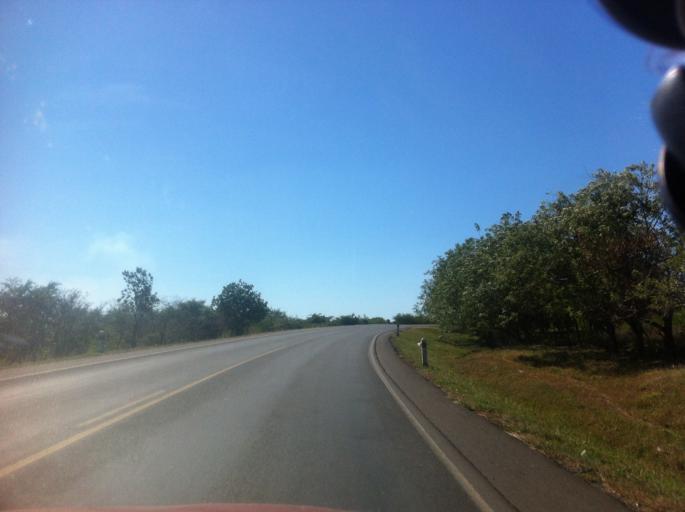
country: NI
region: Managua
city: Tipitapa
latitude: 12.3187
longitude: -85.9826
